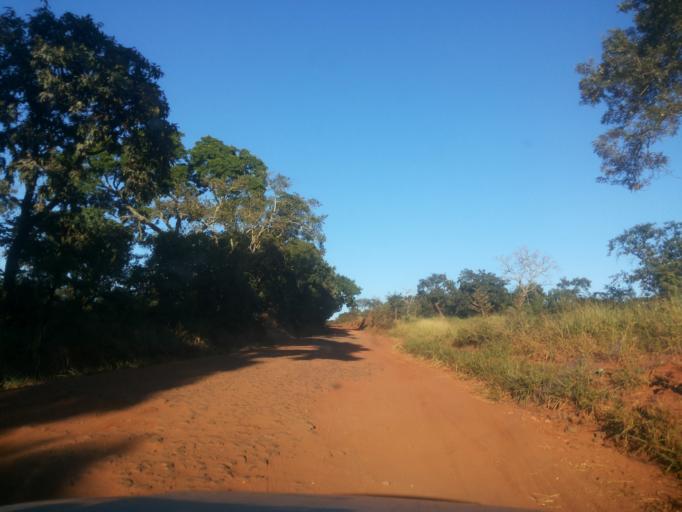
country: BR
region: Minas Gerais
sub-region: Campina Verde
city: Campina Verde
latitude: -19.3209
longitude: -49.7689
